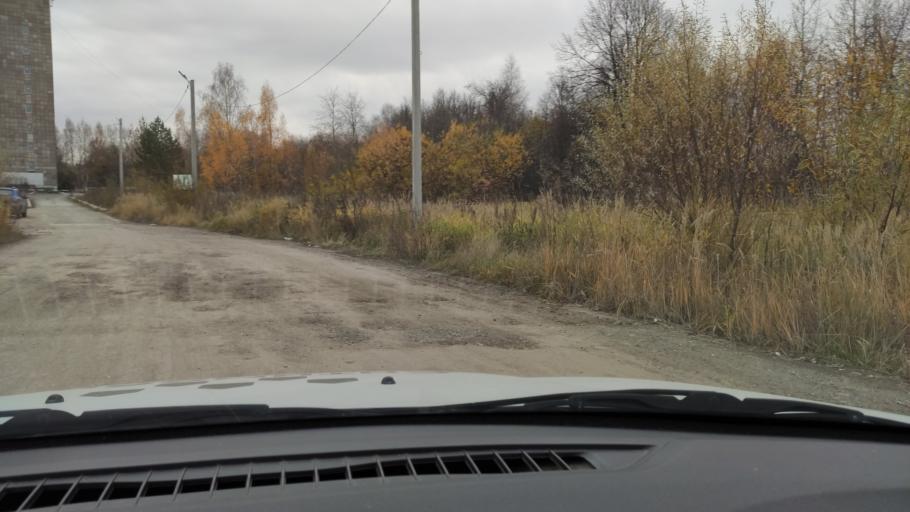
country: RU
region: Perm
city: Froly
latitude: 57.9563
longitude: 56.2739
